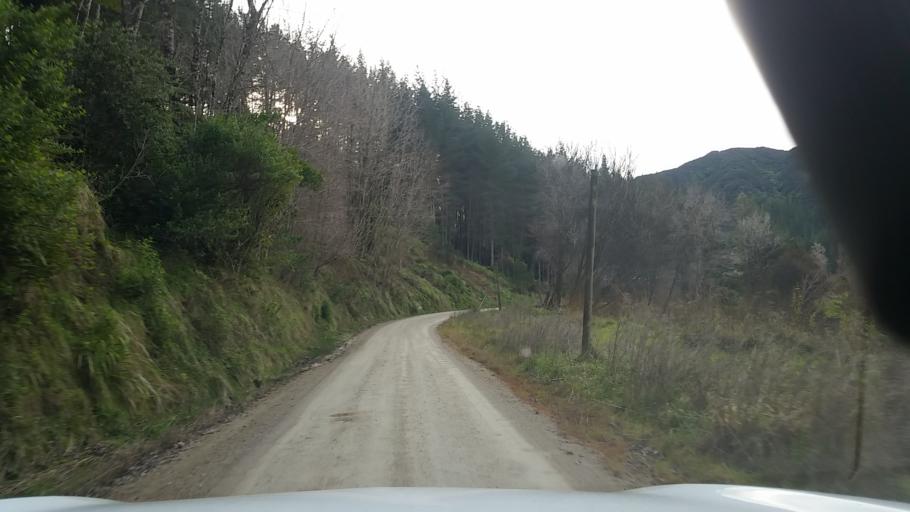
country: NZ
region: Taranaki
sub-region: South Taranaki District
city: Patea
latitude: -39.5780
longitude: 174.8251
